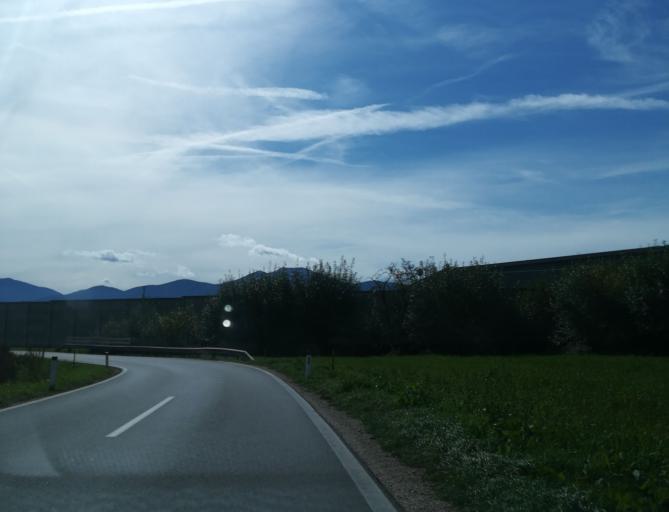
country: AT
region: Styria
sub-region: Politischer Bezirk Murtal
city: Flatschach
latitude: 47.2075
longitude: 14.7573
